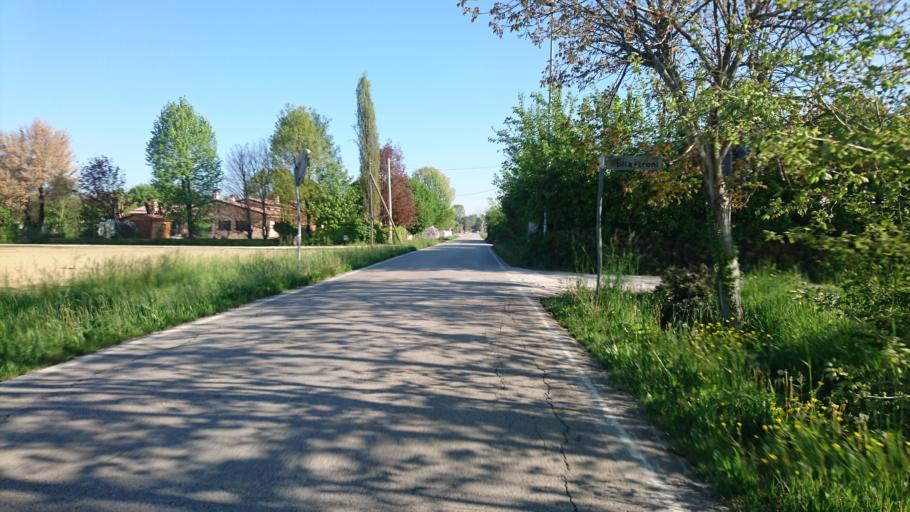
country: IT
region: Veneto
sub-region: Provincia di Padova
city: Massanzago-Ca' Baglioni-San Dono
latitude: 45.5511
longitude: 12.0028
